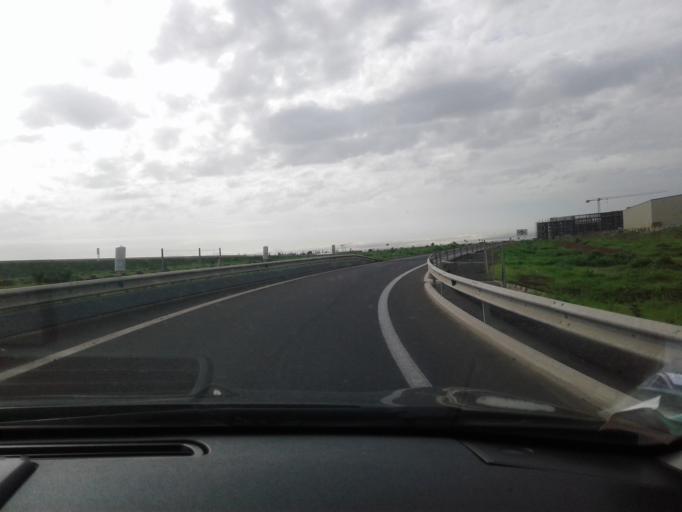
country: SN
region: Thies
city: Thies
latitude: 14.7325
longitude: -17.2093
